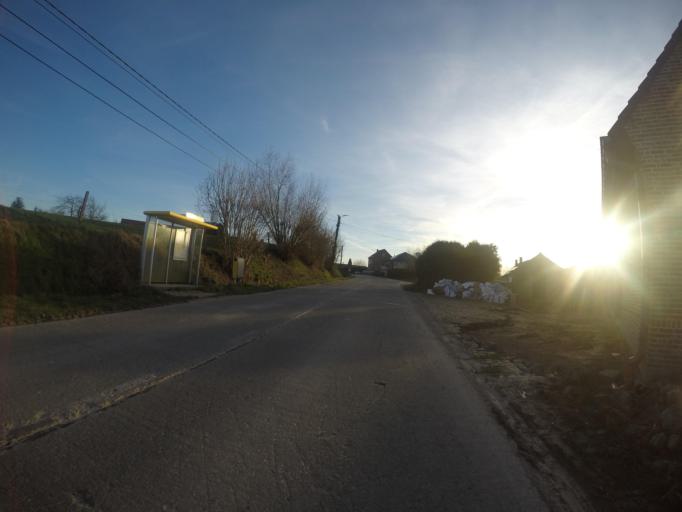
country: BE
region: Flanders
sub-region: Provincie Vlaams-Brabant
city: Pepingen
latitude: 50.7448
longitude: 4.1805
